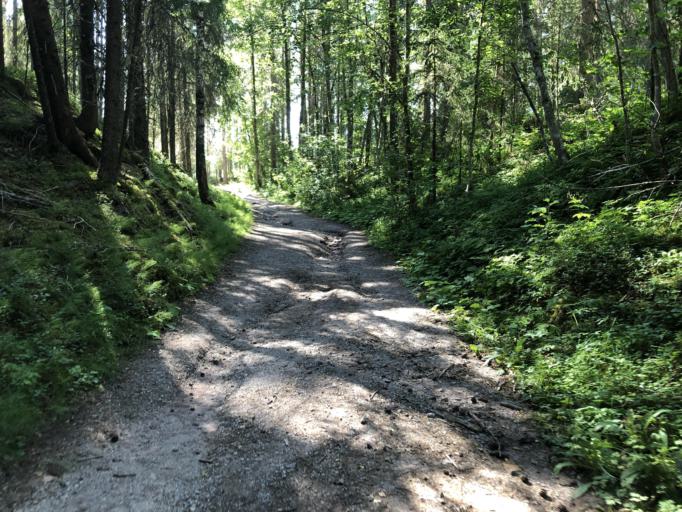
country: SE
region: Dalarna
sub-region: Rattviks Kommun
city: Raettvik
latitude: 60.9237
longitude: 15.1595
